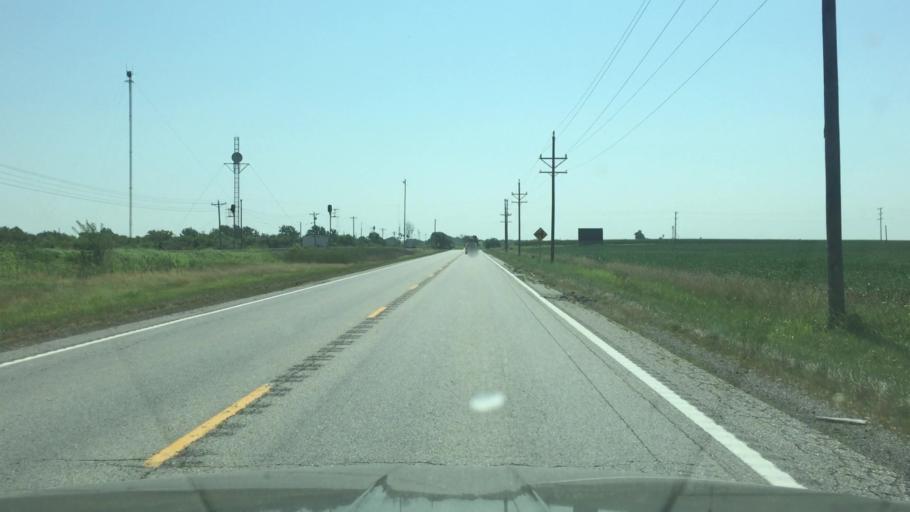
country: US
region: Missouri
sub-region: Moniteau County
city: Tipton
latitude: 38.6641
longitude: -92.8243
